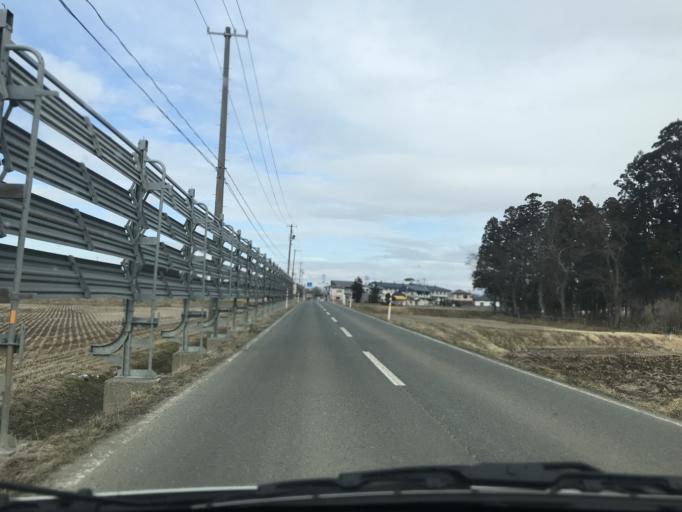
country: JP
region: Iwate
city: Hanamaki
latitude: 39.3442
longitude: 141.0445
